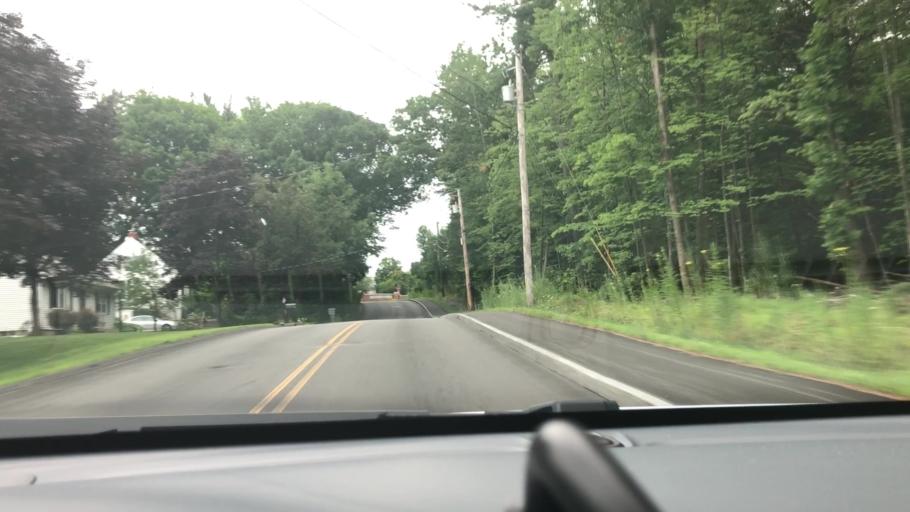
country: US
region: New Hampshire
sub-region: Hillsborough County
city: Pinardville
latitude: 42.9894
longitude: -71.5060
